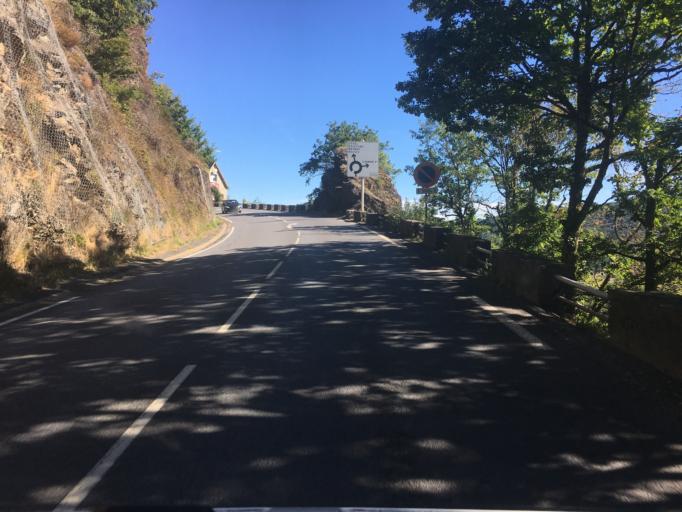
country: FR
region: Limousin
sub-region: Departement de la Correze
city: Bort-les-Orgues
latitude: 45.4096
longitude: 2.4992
